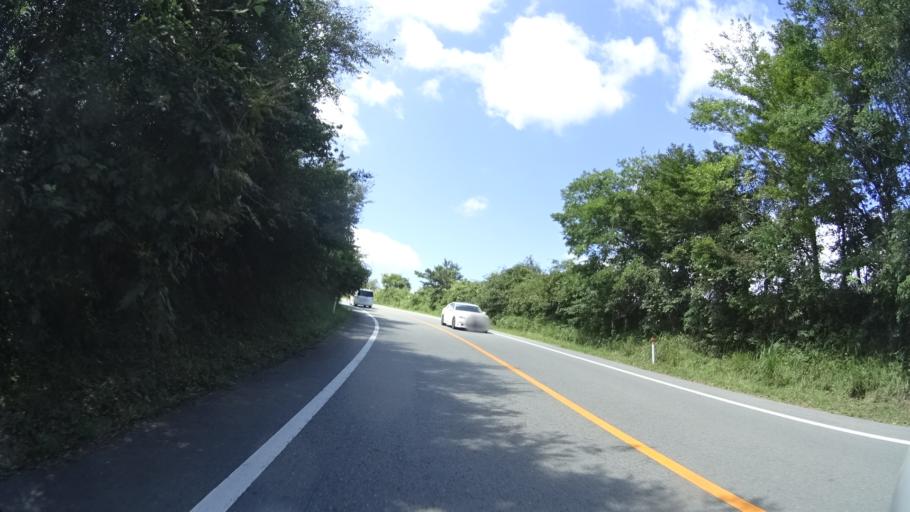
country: JP
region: Kumamoto
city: Aso
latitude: 33.0072
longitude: 131.0997
